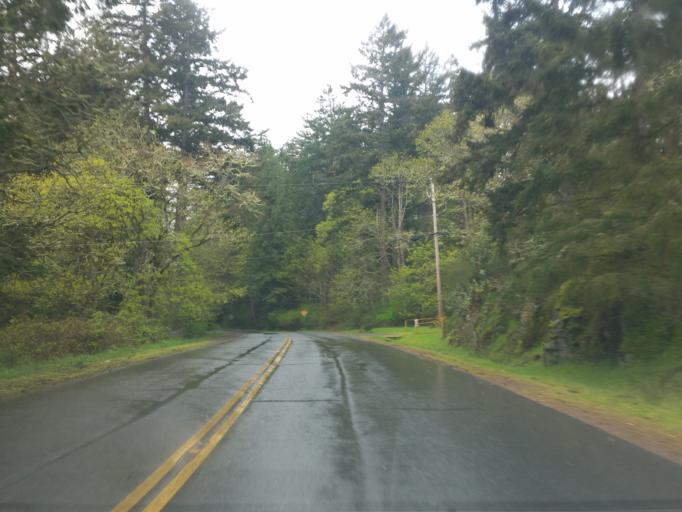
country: CA
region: British Columbia
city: Colwood
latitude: 48.4345
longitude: -123.4541
